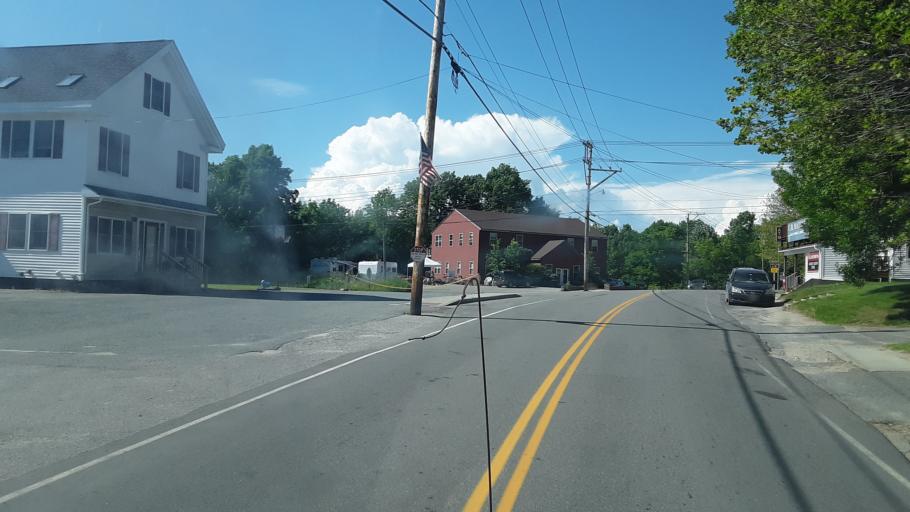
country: US
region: Maine
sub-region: Washington County
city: Cherryfield
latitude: 44.6067
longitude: -67.9265
